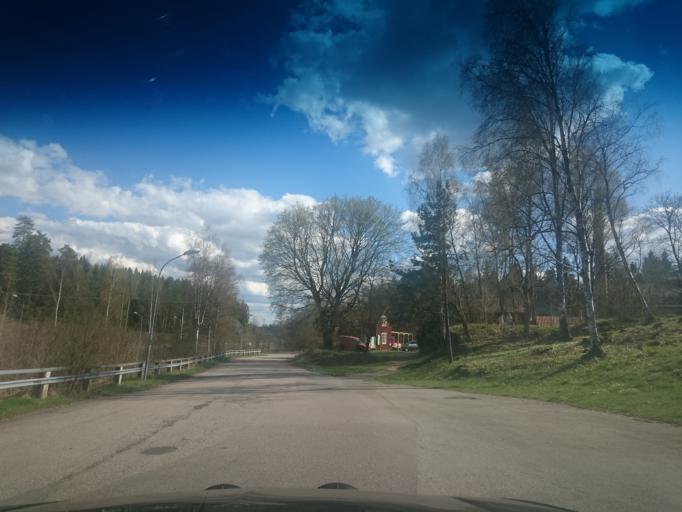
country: SE
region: Kronoberg
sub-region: Vaxjo Kommun
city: Braas
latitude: 57.2206
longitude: 15.1442
